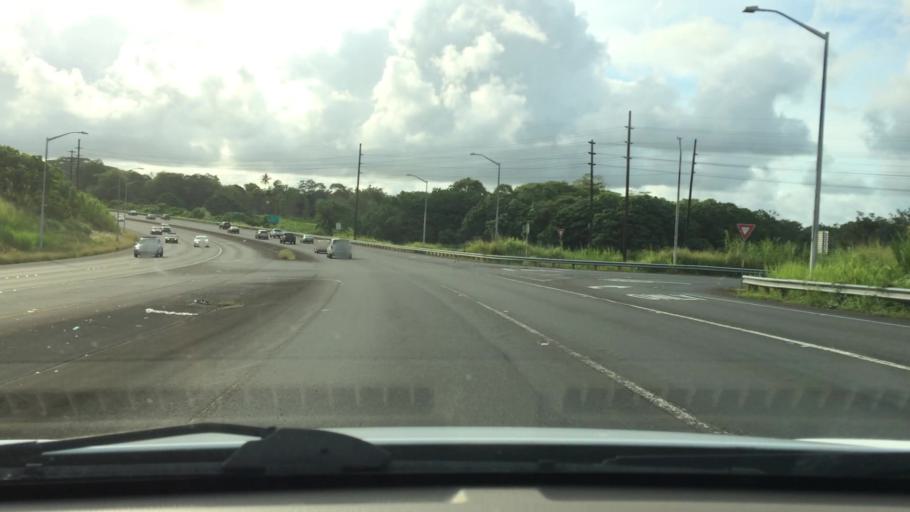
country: US
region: Hawaii
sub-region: Hawaii County
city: Kea'au
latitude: 19.6317
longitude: -155.0353
